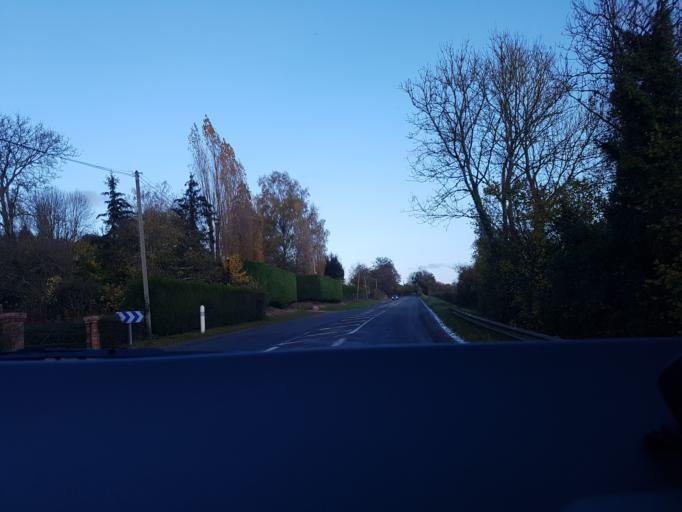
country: FR
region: Lower Normandy
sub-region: Departement du Calvados
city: Dozule
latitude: 49.2504
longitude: 0.0270
